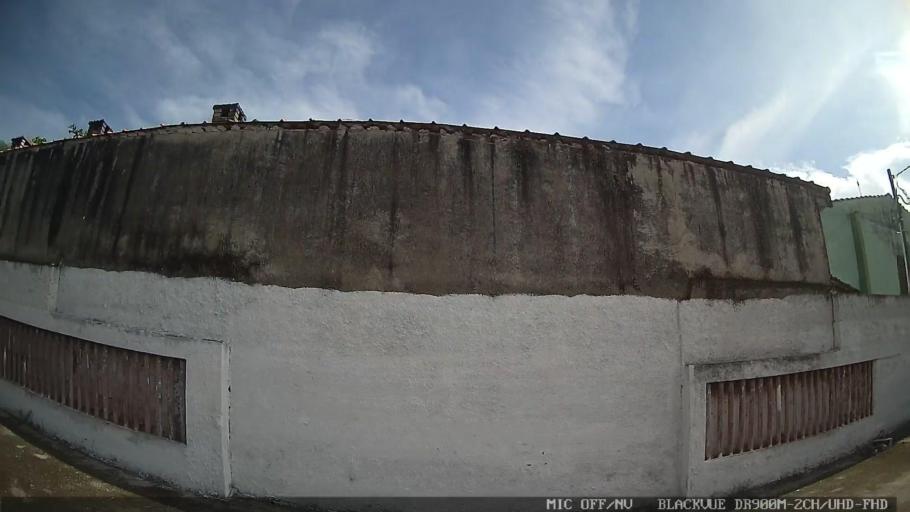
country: BR
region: Sao Paulo
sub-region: Itanhaem
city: Itanhaem
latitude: -24.1651
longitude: -46.7671
